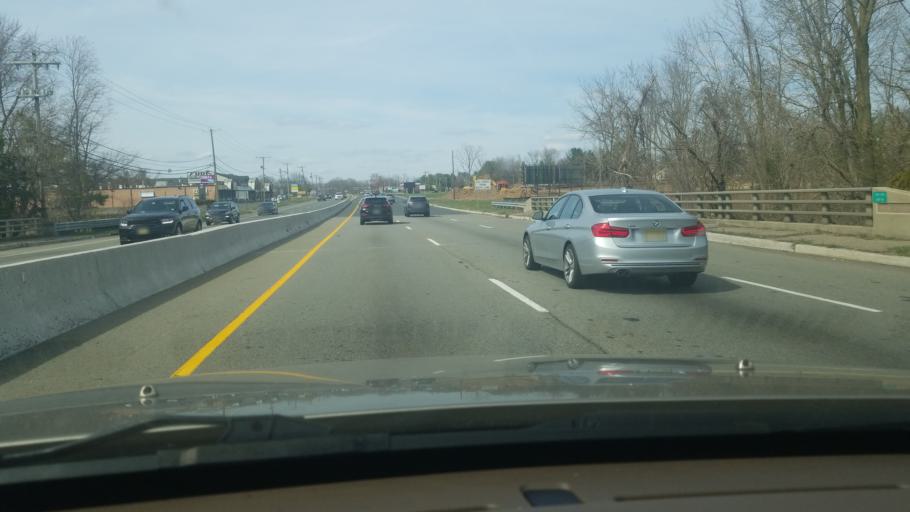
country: US
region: New Jersey
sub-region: Monmouth County
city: Freehold
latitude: 40.2042
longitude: -74.2561
